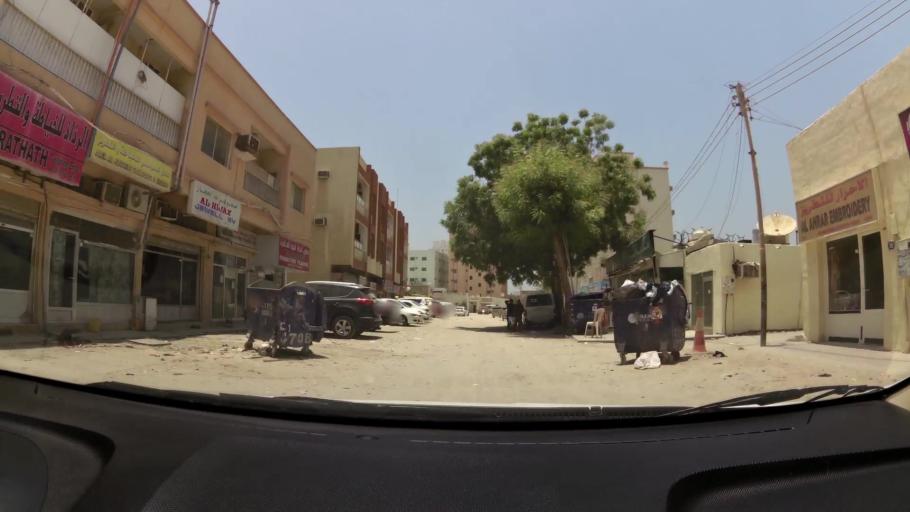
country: AE
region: Ajman
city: Ajman
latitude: 25.4130
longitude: 55.4409
